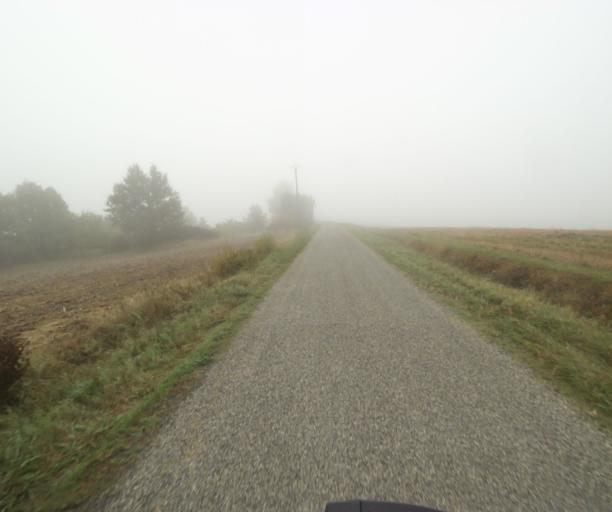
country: FR
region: Midi-Pyrenees
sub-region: Departement de la Haute-Garonne
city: Villemur-sur-Tarn
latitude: 43.8977
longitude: 1.4789
